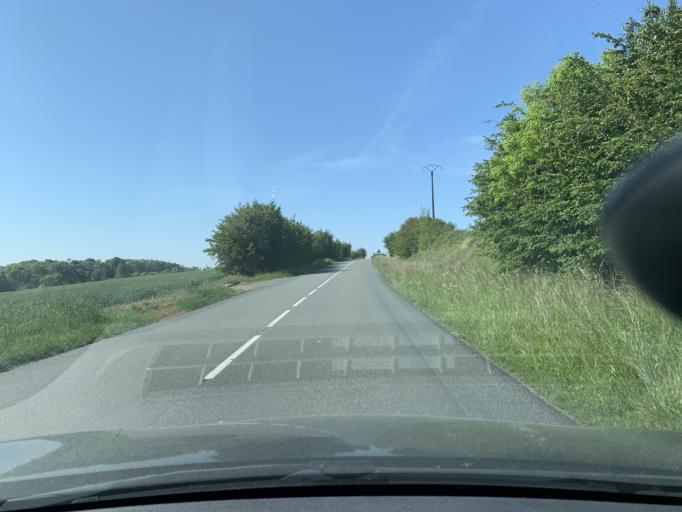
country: FR
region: Nord-Pas-de-Calais
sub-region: Departement du Nord
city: Masnieres
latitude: 50.0818
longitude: 3.2168
